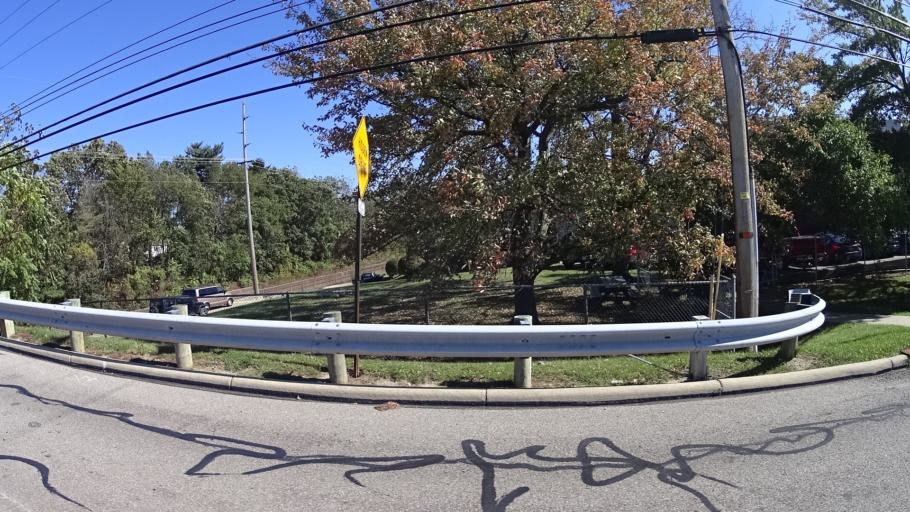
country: US
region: Ohio
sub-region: Lorain County
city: Amherst
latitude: 41.3946
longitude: -82.2178
